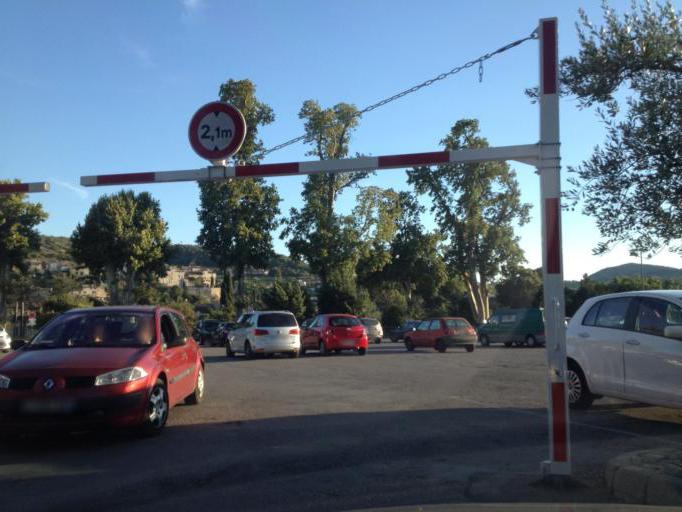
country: FR
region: Provence-Alpes-Cote d'Azur
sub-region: Departement du Vaucluse
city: Vaison-la-Romaine
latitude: 44.2433
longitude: 5.0723
